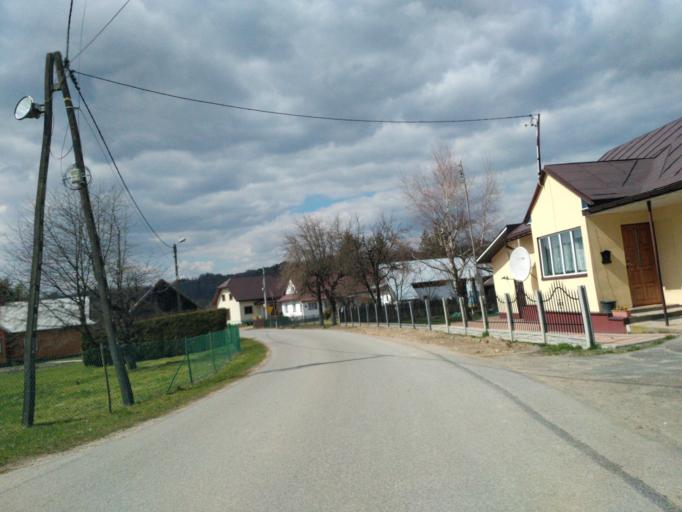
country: PL
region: Subcarpathian Voivodeship
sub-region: Powiat sanocki
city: Tyrawa Woloska
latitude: 49.6455
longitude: 22.2998
